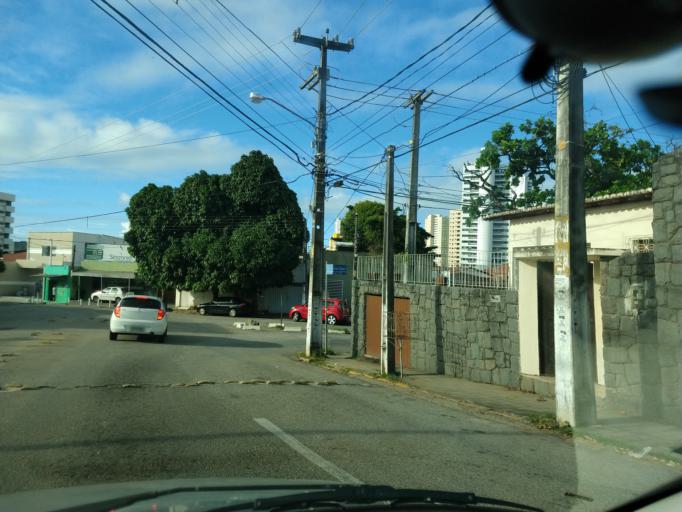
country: BR
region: Rio Grande do Norte
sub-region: Natal
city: Natal
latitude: -5.7950
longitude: -35.2091
